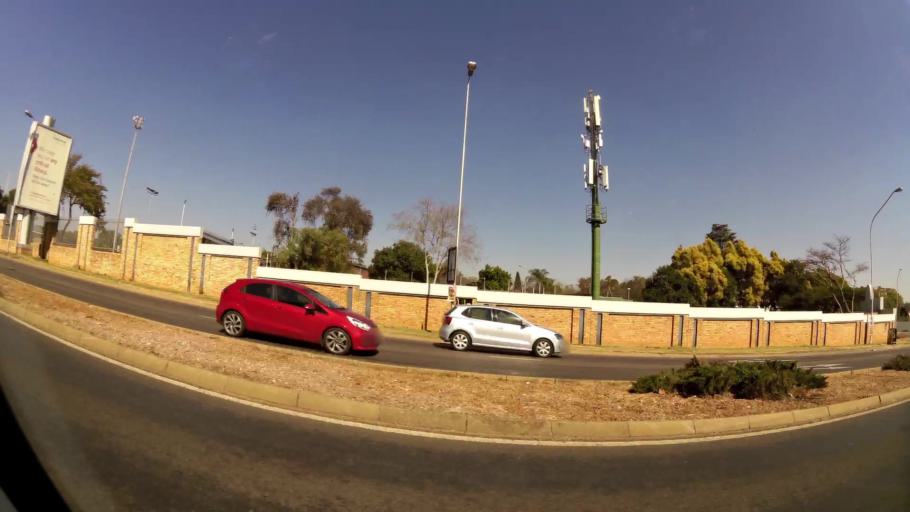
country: ZA
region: Gauteng
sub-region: City of Tshwane Metropolitan Municipality
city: Pretoria
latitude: -25.7626
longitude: 28.2564
